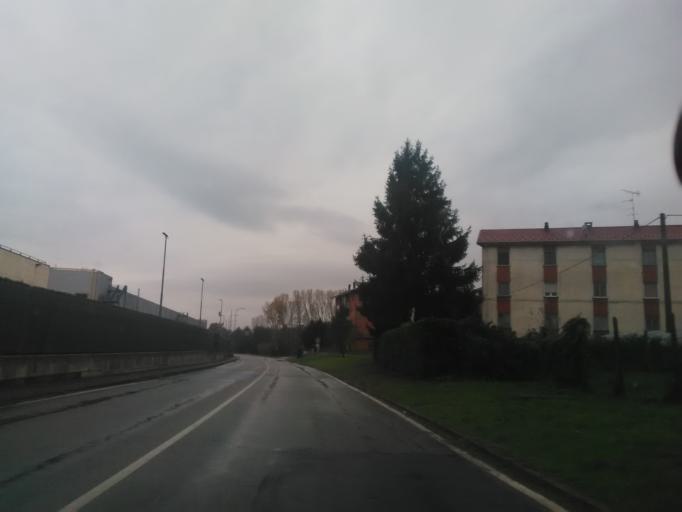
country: IT
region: Piedmont
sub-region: Provincia di Vercelli
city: Gattinara
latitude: 45.6125
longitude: 8.3615
